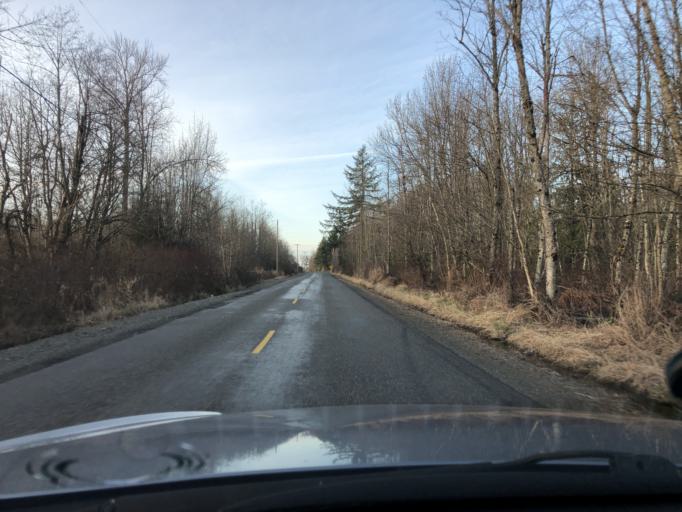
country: US
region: Washington
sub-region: Pierce County
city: Bonney Lake
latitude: 47.2184
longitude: -122.1228
